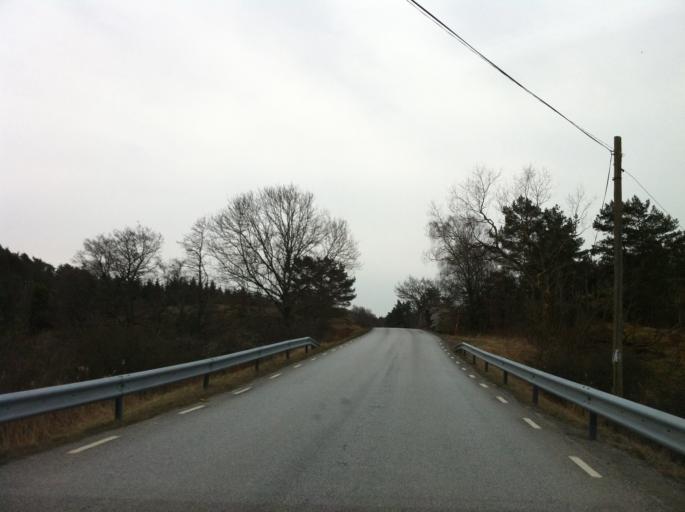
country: SE
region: Vaestra Goetaland
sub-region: Orust
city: Henan
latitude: 58.2600
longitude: 11.6781
